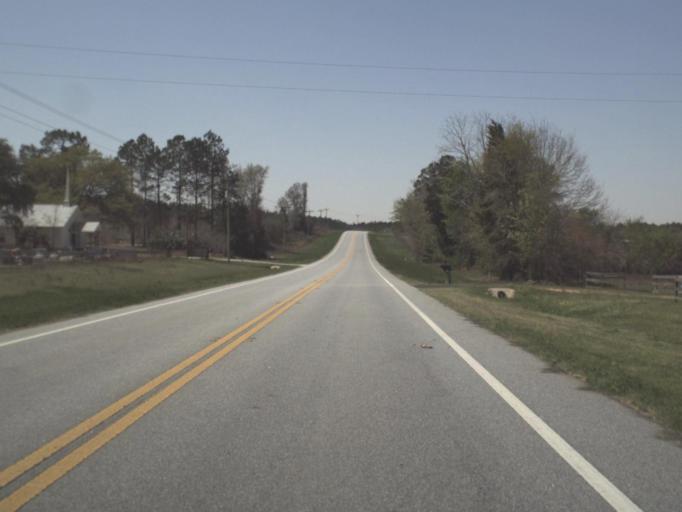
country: US
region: Alabama
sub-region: Geneva County
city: Geneva
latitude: 30.9432
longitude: -85.7788
